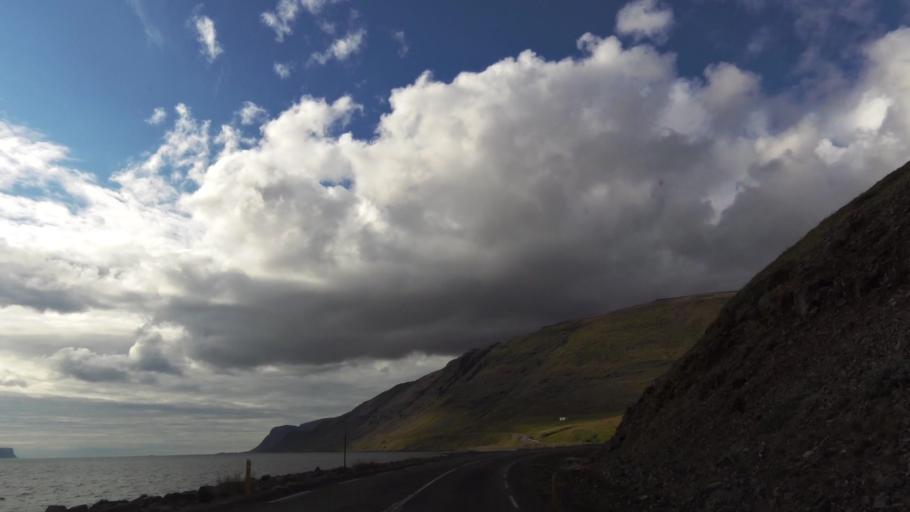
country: IS
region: West
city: Olafsvik
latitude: 65.5472
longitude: -23.8876
